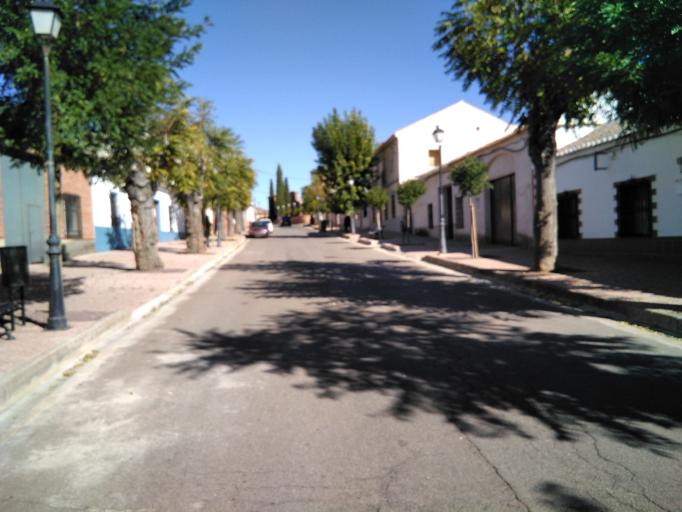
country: ES
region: Castille-La Mancha
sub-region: Provincia de Ciudad Real
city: Ballesteros de Calatrava
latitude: 38.8356
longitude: -3.9437
